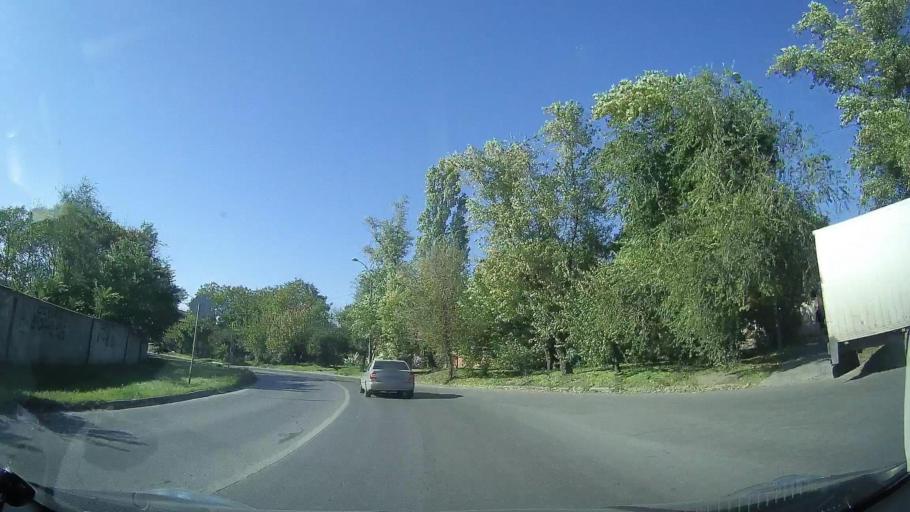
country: RU
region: Rostov
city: Rostov-na-Donu
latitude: 47.2259
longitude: 39.6816
